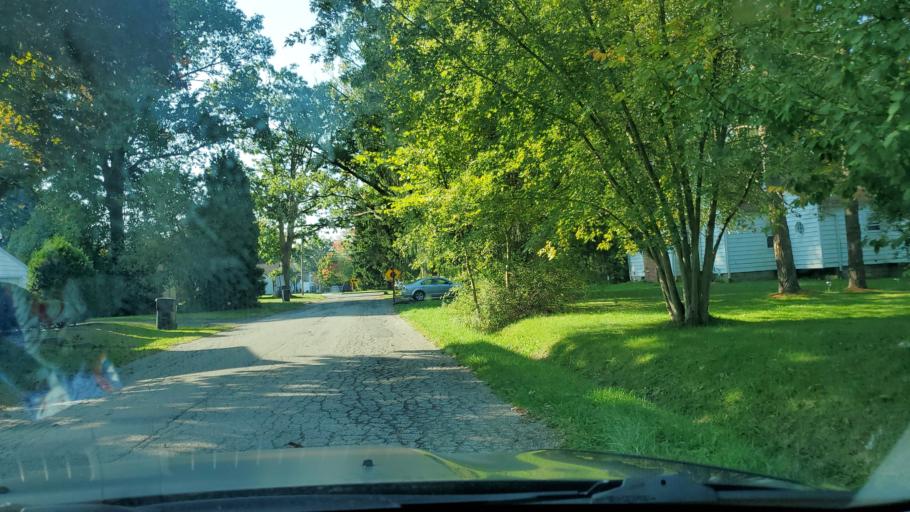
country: US
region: Ohio
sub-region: Mahoning County
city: Boardman
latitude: 41.0446
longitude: -80.6502
